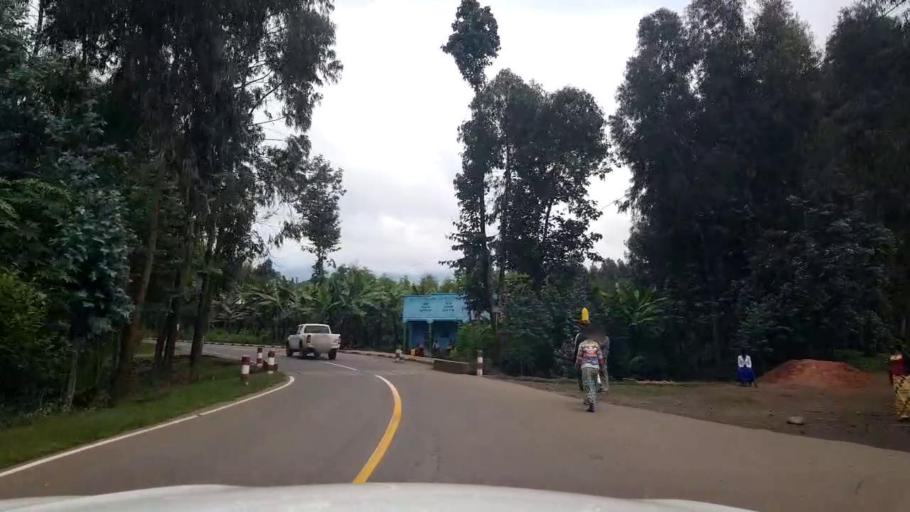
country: RW
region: Northern Province
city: Musanze
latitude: -1.4536
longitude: 29.6083
